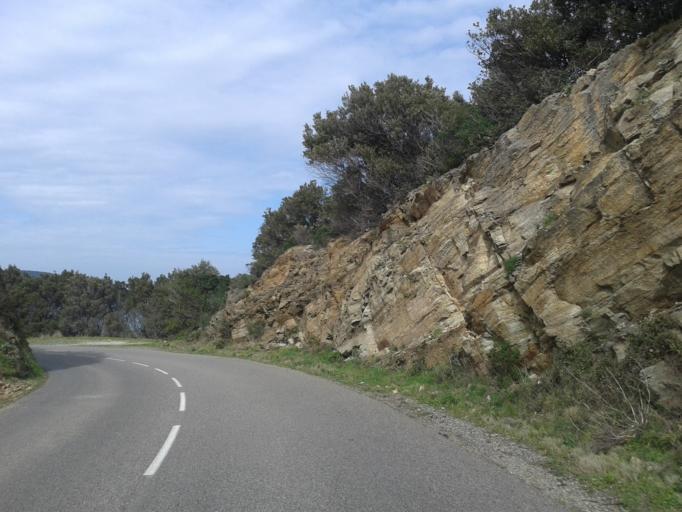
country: FR
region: Corsica
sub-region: Departement de la Haute-Corse
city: Brando
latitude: 42.9423
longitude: 9.4649
